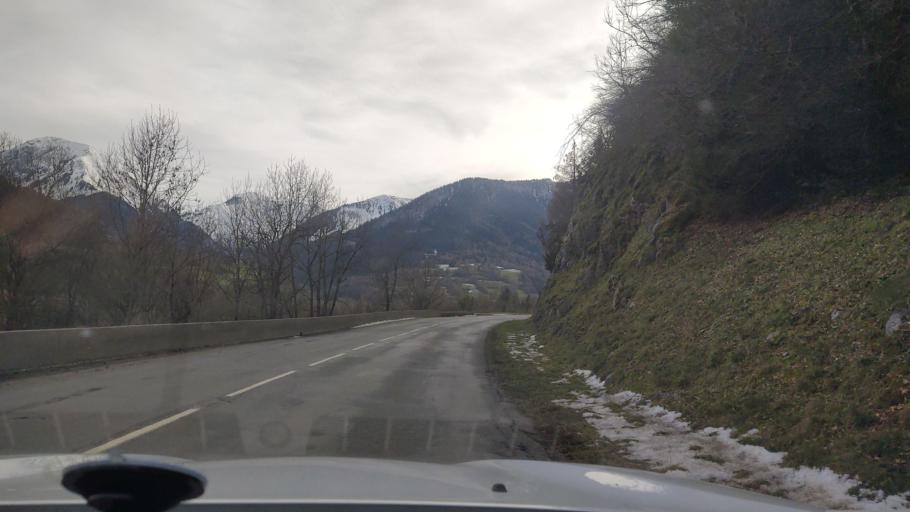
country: FR
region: Rhone-Alpes
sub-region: Departement de la Savoie
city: Gresy-sur-Isere
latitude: 45.6610
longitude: 6.1621
